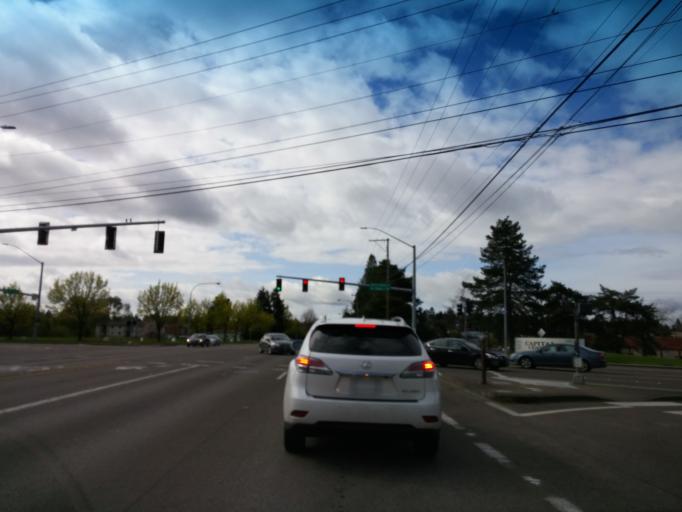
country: US
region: Oregon
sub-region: Washington County
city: Rockcreek
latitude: 45.5281
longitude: -122.8676
